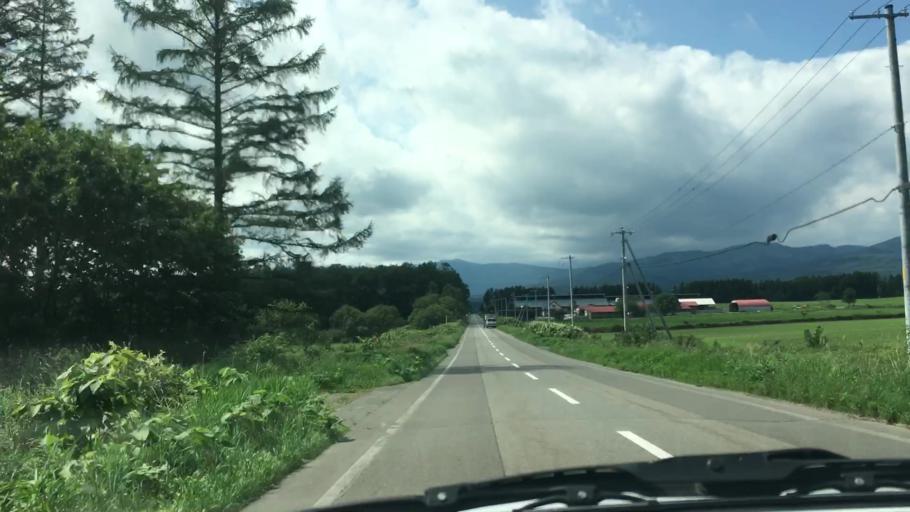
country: JP
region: Hokkaido
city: Otofuke
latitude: 43.2805
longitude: 143.3377
